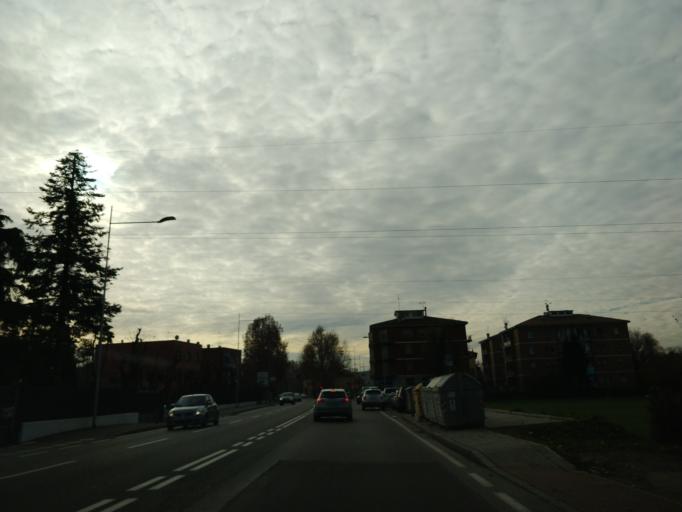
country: IT
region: Emilia-Romagna
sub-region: Provincia di Bologna
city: Progresso
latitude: 44.5309
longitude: 11.3671
